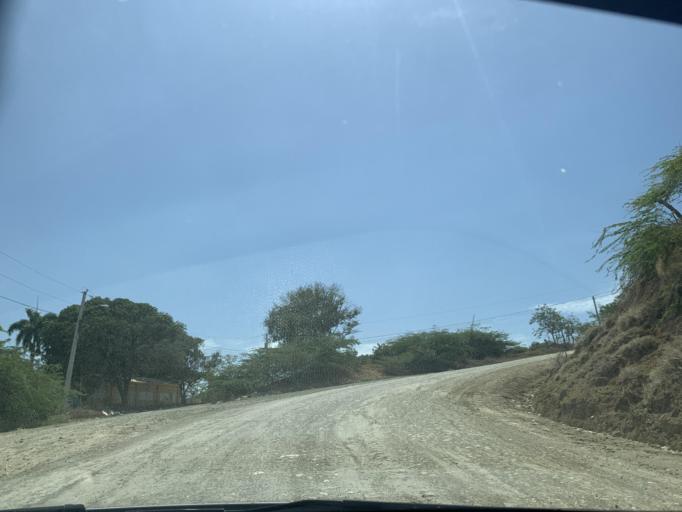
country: DO
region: Puerto Plata
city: Imbert
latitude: 19.8678
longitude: -70.8211
